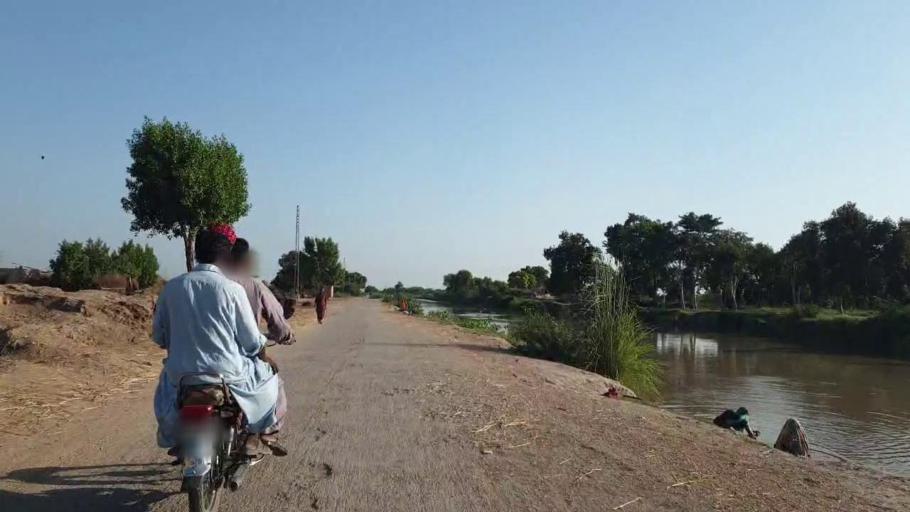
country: PK
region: Sindh
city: Hyderabad
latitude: 25.3077
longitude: 68.4332
